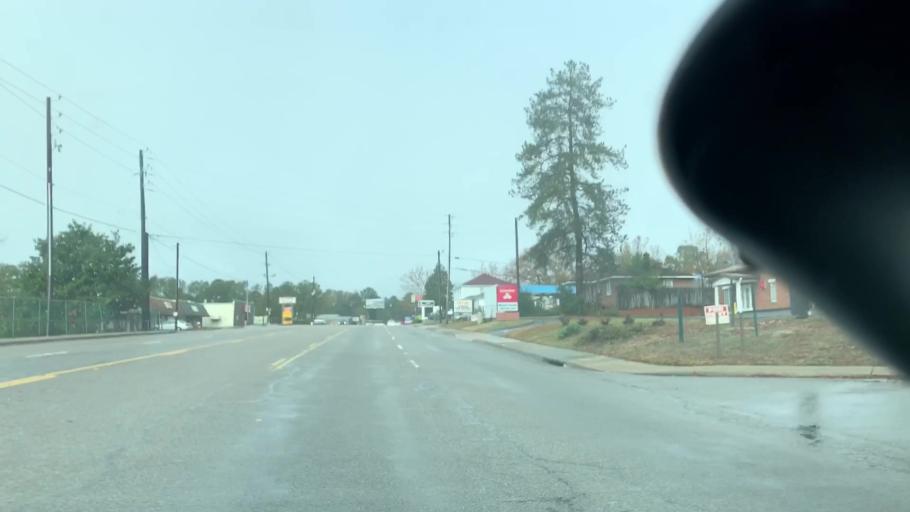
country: US
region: South Carolina
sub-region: Richland County
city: Woodfield
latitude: 34.0434
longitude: -80.9405
